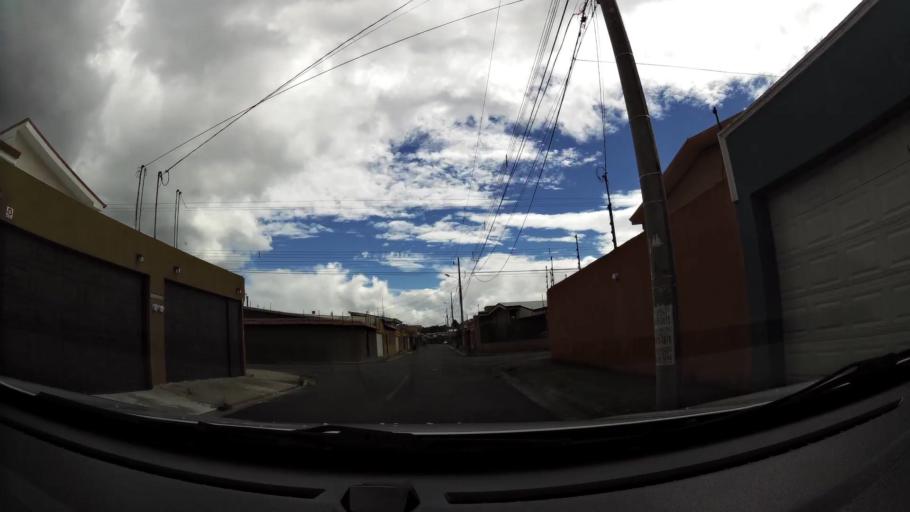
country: CR
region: Cartago
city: Concepcion
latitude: 9.9254
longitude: -84.0019
